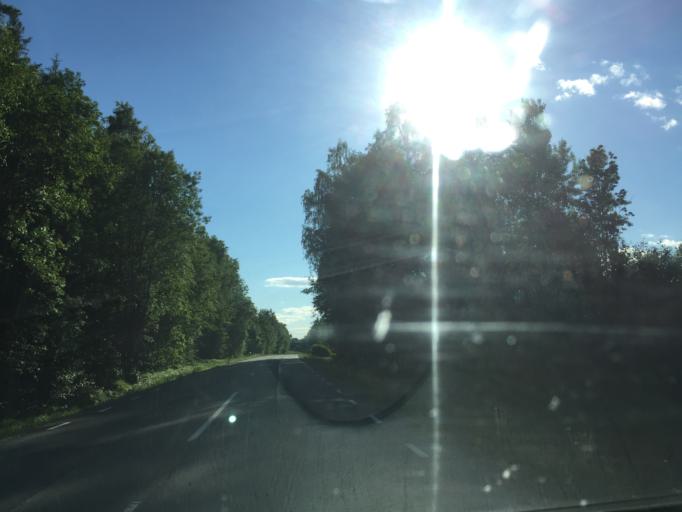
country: SE
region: OErebro
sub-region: Hallsbergs Kommun
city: Skollersta
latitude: 59.2023
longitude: 15.2893
